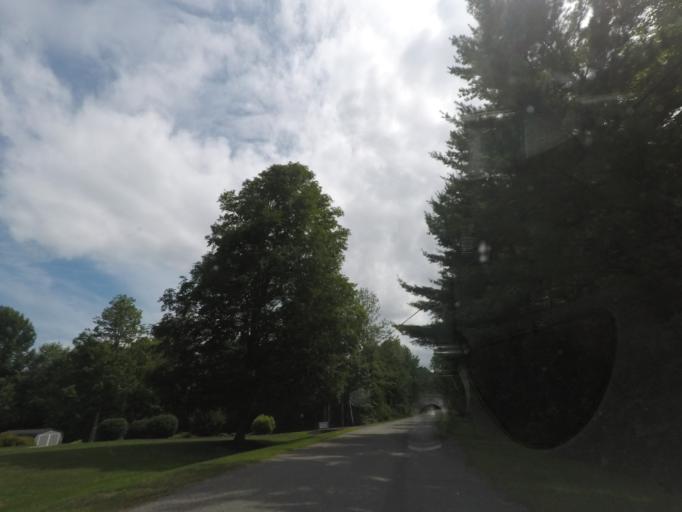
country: US
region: New York
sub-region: Saratoga County
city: Stillwater
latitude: 43.0147
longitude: -73.6458
